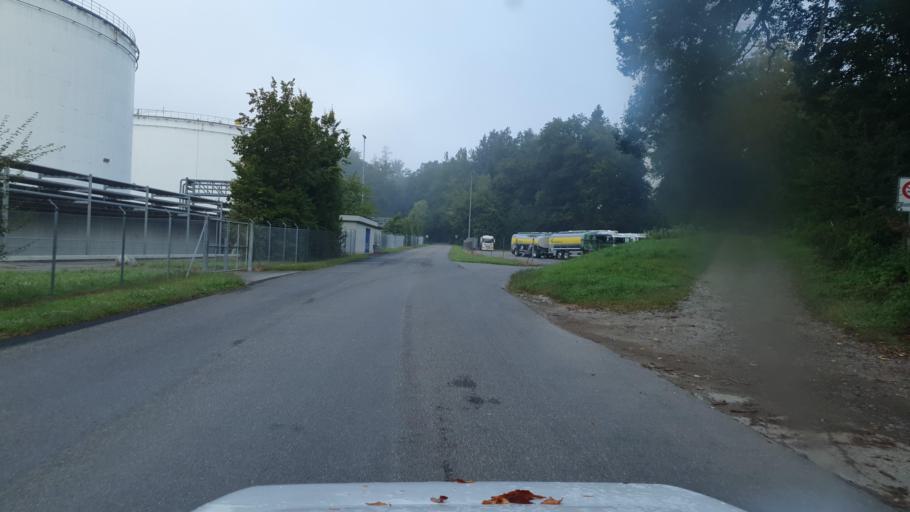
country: CH
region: Aargau
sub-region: Bezirk Baden
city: Mellingen
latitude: 47.4307
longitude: 8.2681
